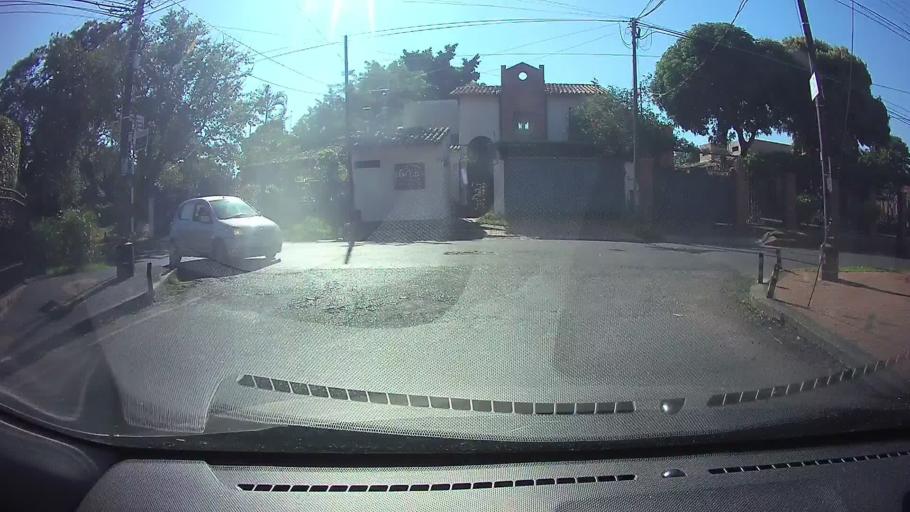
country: PY
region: Central
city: Fernando de la Mora
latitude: -25.2671
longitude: -57.5149
